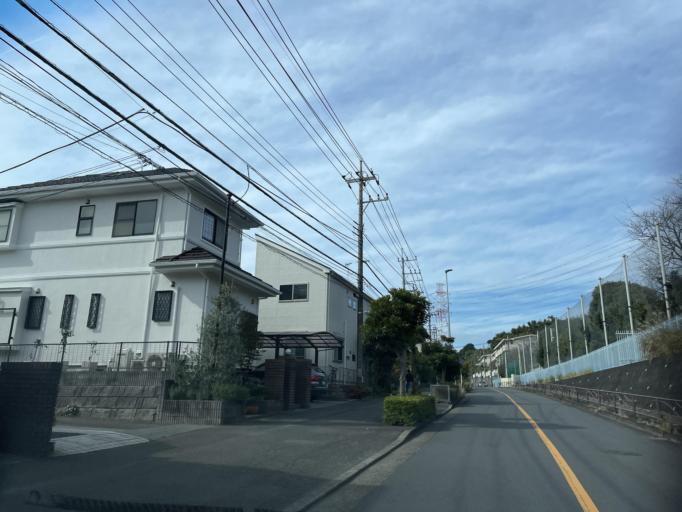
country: JP
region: Tokyo
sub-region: Machida-shi
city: Machida
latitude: 35.6114
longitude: 139.4764
